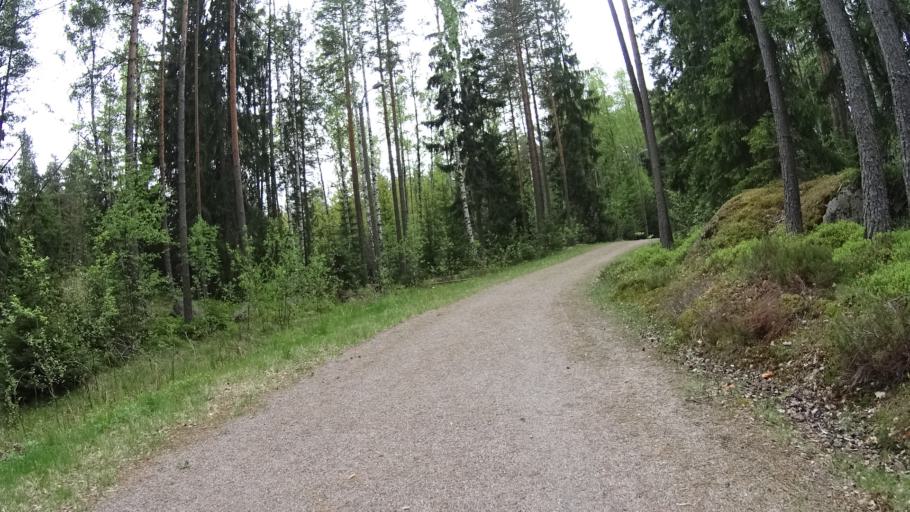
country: FI
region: Uusimaa
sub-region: Helsinki
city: Espoo
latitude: 60.2344
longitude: 24.6783
